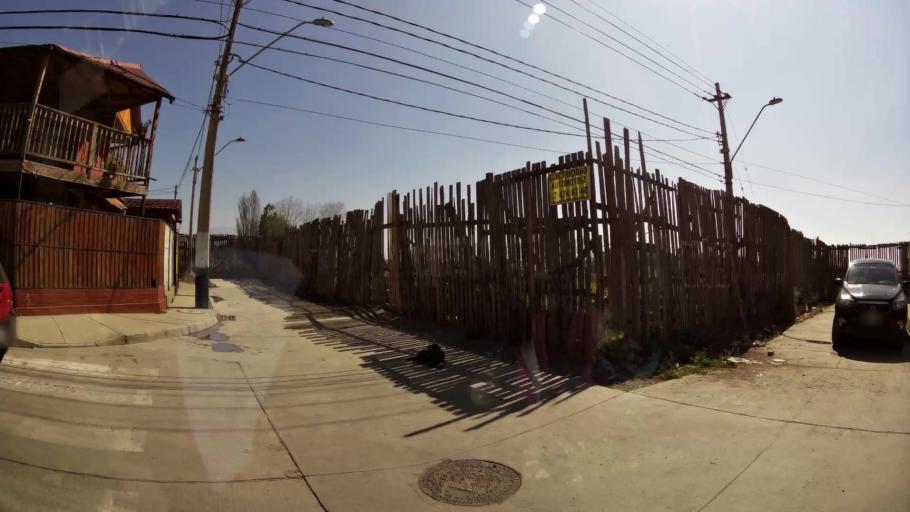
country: CL
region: Santiago Metropolitan
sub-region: Provincia de Santiago
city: Lo Prado
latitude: -33.3524
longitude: -70.7532
